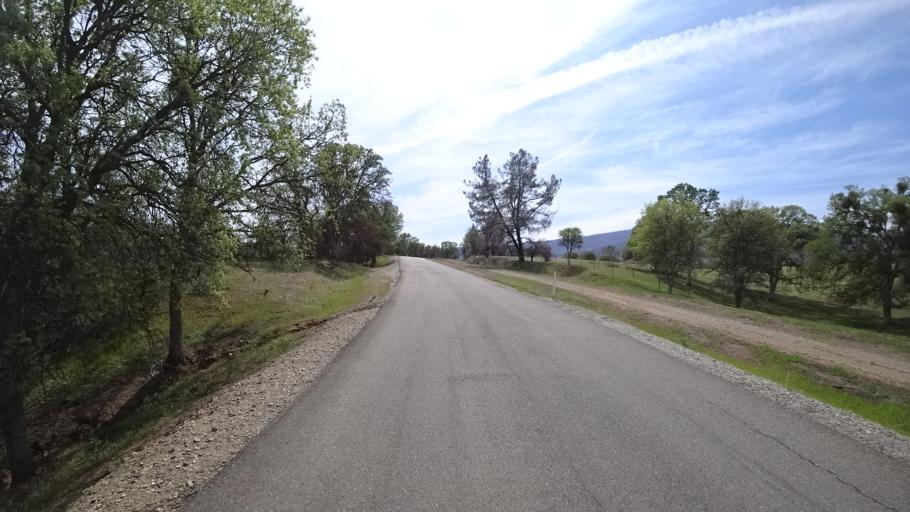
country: US
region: California
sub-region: Glenn County
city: Willows
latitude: 39.5792
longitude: -122.5993
